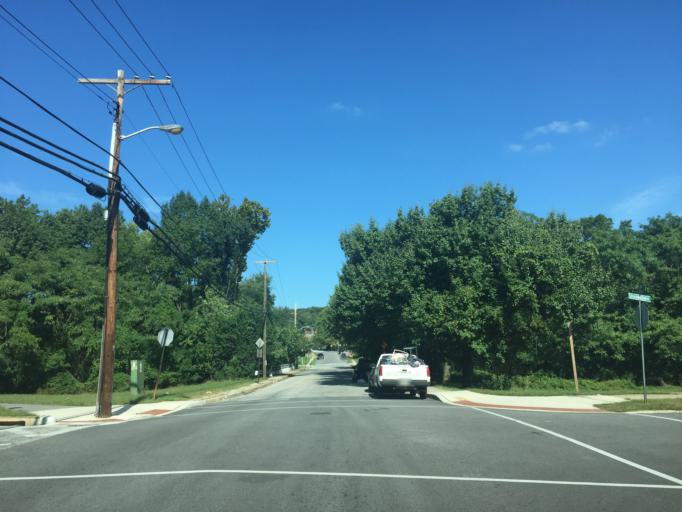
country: US
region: Maryland
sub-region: Baltimore County
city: Rosedale
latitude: 39.3228
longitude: -76.5622
